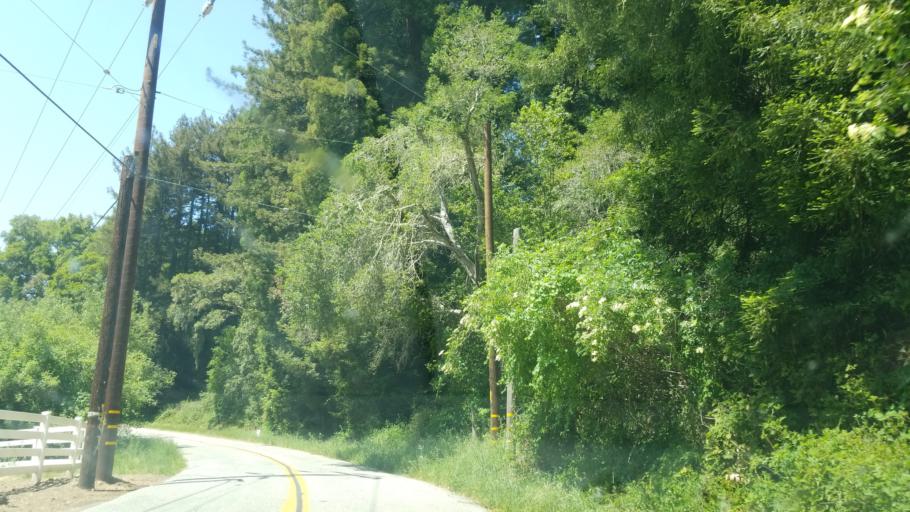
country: US
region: California
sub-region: Santa Cruz County
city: Amesti
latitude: 37.0154
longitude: -121.7541
